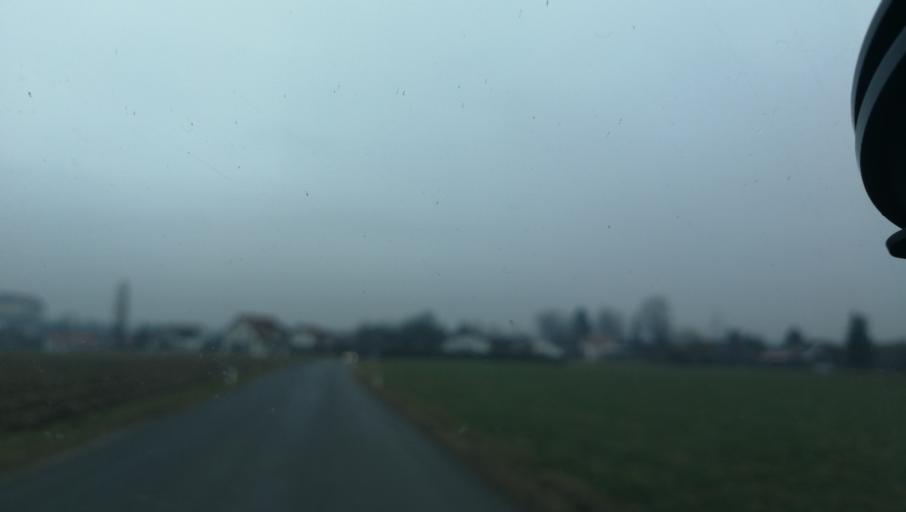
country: AT
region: Styria
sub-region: Politischer Bezirk Deutschlandsberg
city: Stainz
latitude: 46.8938
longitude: 15.2511
